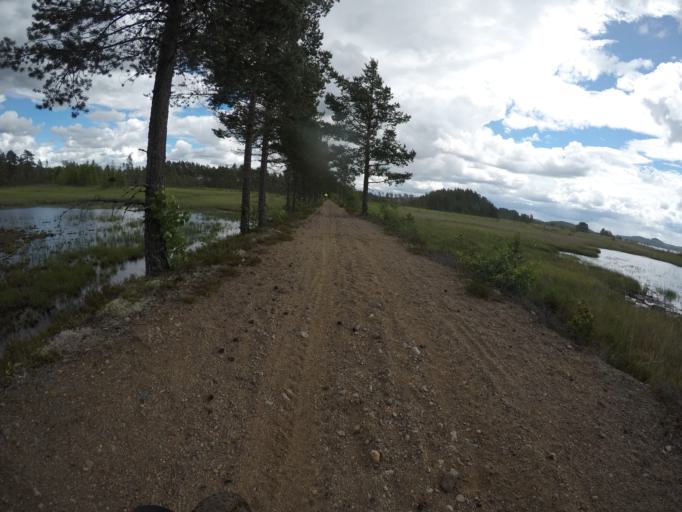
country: SE
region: Vaermland
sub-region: Filipstads Kommun
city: Lesjofors
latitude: 60.1405
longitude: 14.2529
